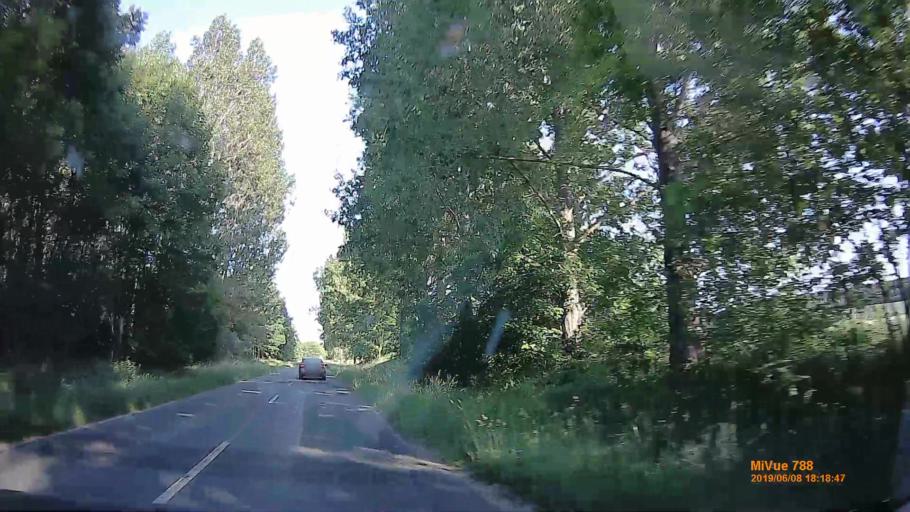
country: HU
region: Vas
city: Buk
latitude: 47.3702
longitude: 16.7333
